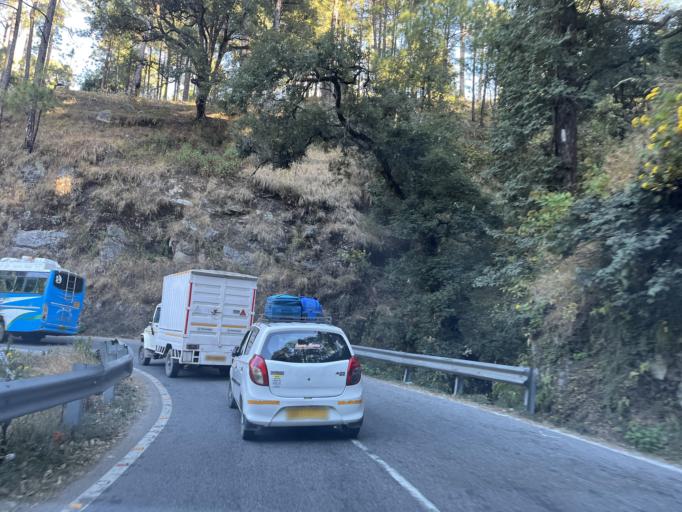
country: IN
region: Uttarakhand
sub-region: Naini Tal
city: Bhowali
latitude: 29.3986
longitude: 79.5102
